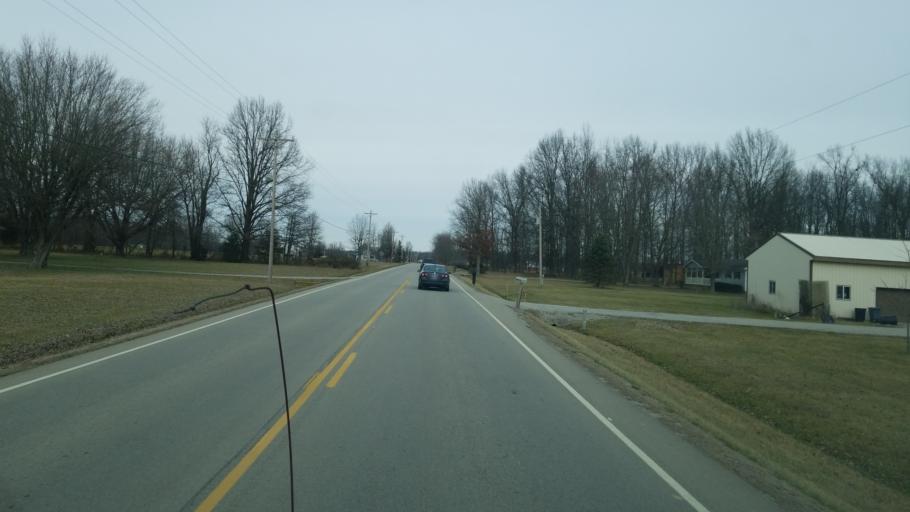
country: US
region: Ohio
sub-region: Highland County
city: Hillsboro
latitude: 39.0873
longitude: -83.6823
